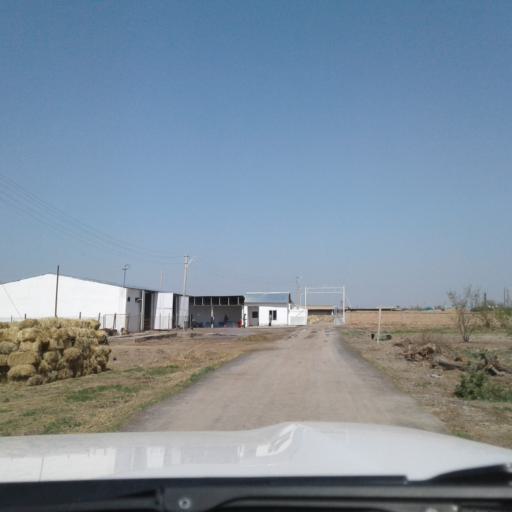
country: TM
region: Lebap
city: Turkmenabat
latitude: 38.9596
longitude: 63.6453
